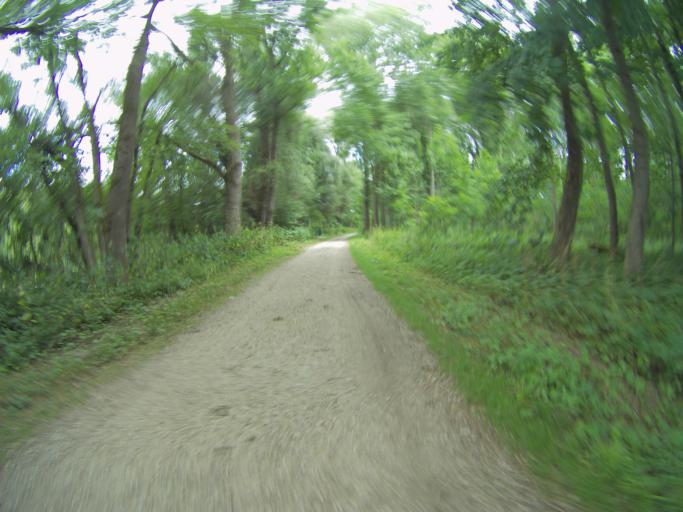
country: DE
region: Bavaria
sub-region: Upper Bavaria
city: Freising
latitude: 48.3958
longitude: 11.7500
